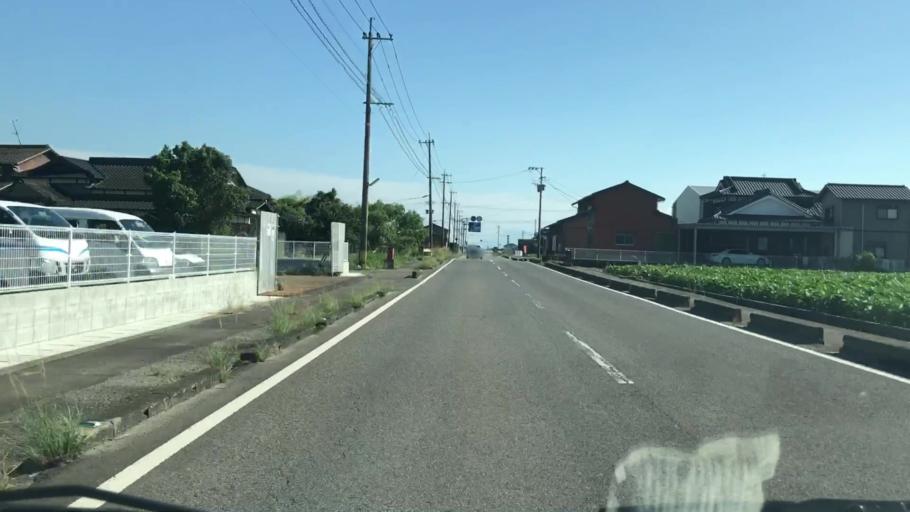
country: JP
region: Saga Prefecture
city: Okawa
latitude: 33.2000
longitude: 130.3351
